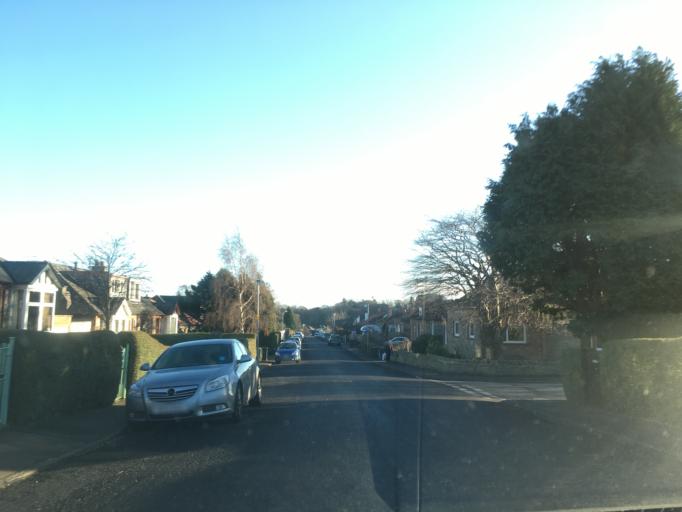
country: GB
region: Scotland
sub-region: Edinburgh
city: Colinton
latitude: 55.9595
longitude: -3.2577
